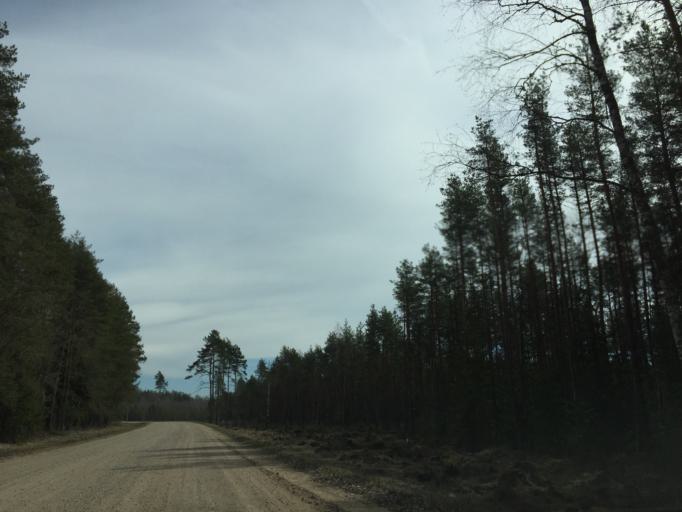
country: LV
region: Valkas Rajons
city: Valka
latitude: 57.8149
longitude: 25.8537
